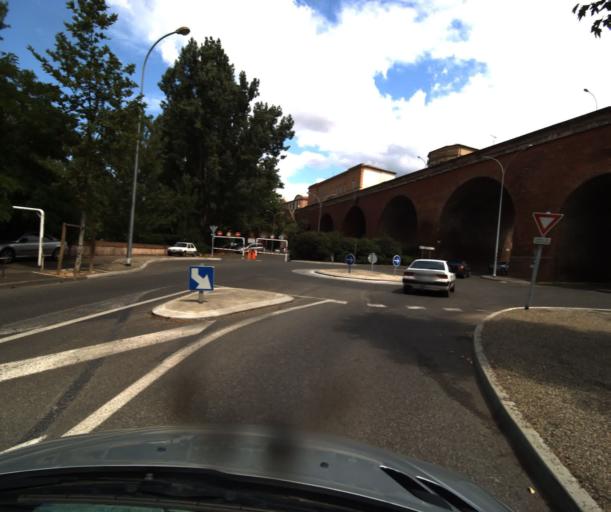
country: FR
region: Midi-Pyrenees
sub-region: Departement du Tarn-et-Garonne
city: Montauban
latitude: 44.0185
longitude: 1.3508
